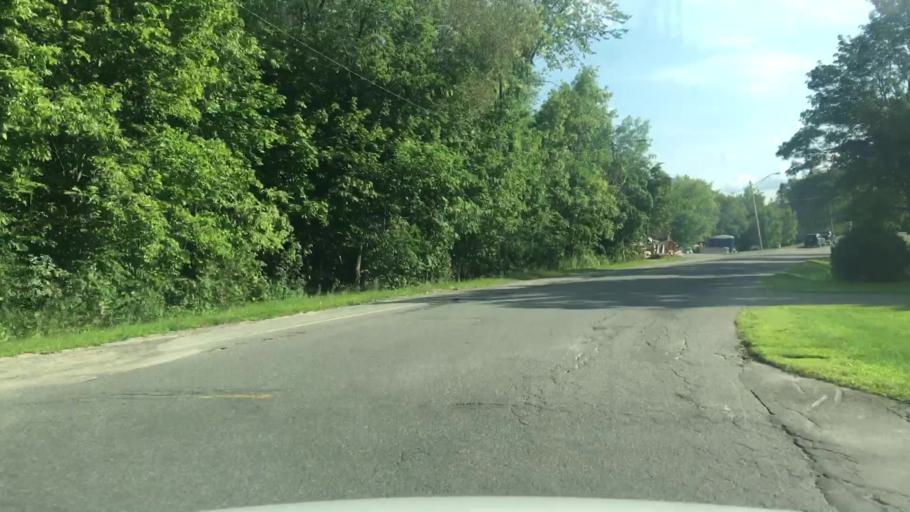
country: US
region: Maine
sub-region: Kennebec County
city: Waterville
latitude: 44.5530
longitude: -69.6412
